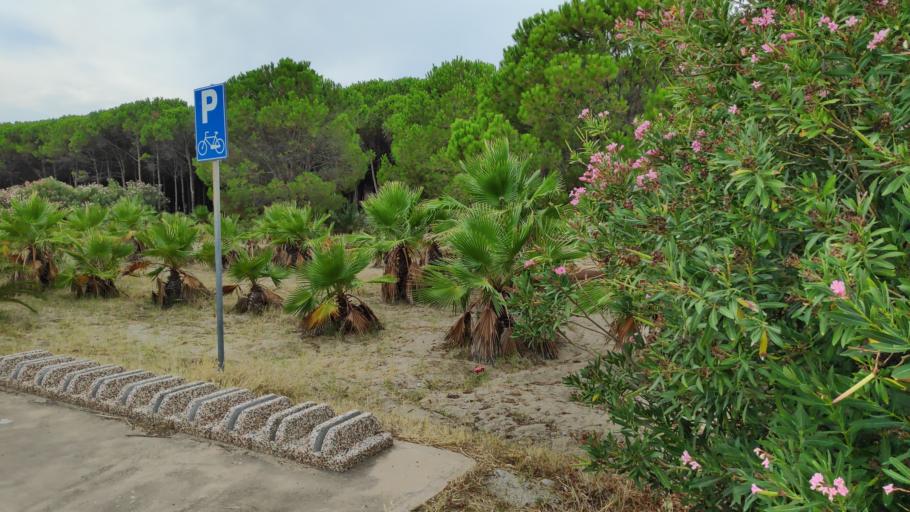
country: IT
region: Calabria
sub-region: Provincia di Catanzaro
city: Soverato Marina
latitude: 38.6820
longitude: 16.5574
